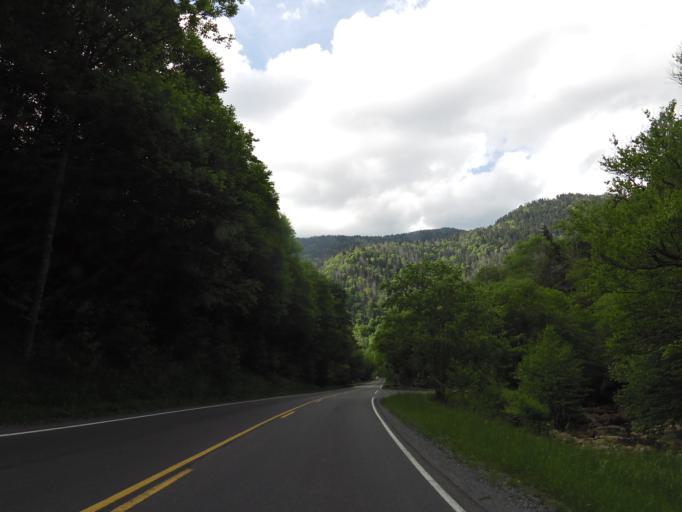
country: US
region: Tennessee
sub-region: Sevier County
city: Gatlinburg
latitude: 35.6319
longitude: -83.4610
